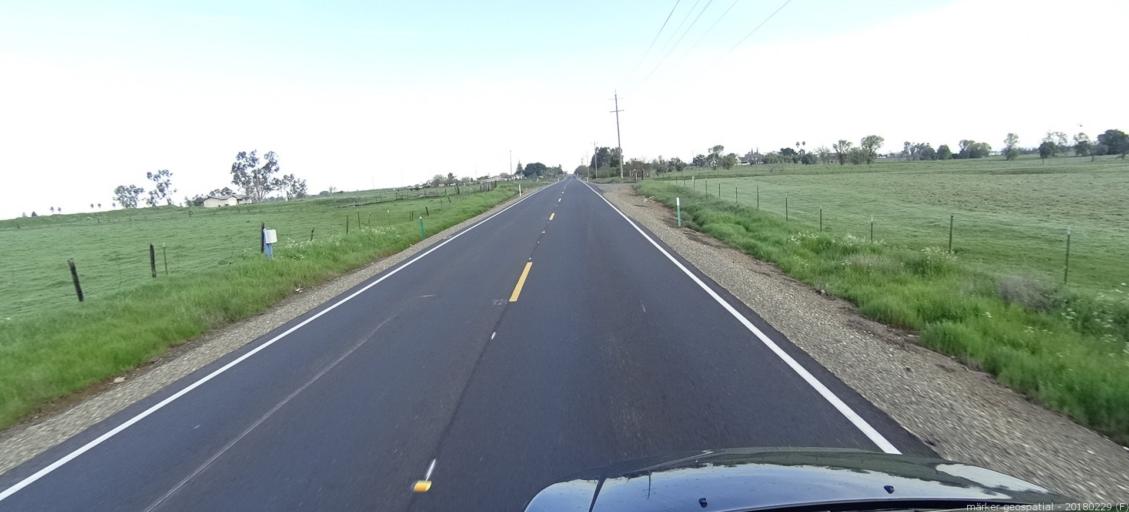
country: US
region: California
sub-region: Sacramento County
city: Vineyard
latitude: 38.5063
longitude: -121.2979
